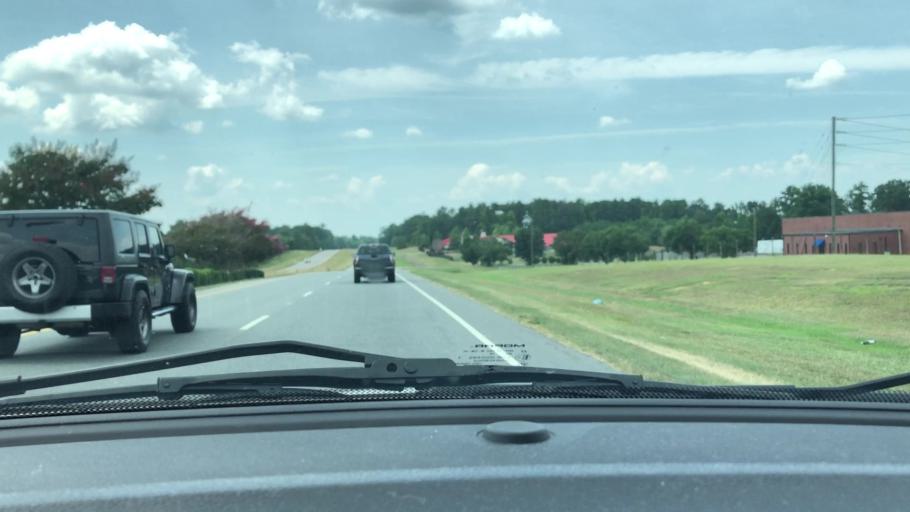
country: US
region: North Carolina
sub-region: Chatham County
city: Farmville
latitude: 35.5211
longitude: -79.2221
